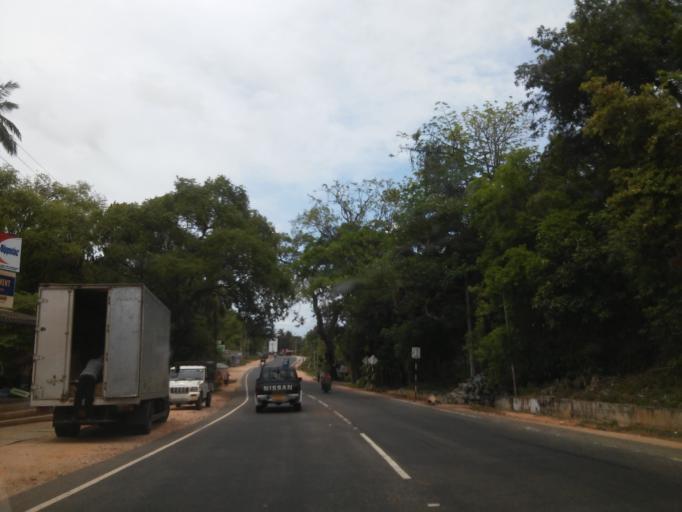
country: LK
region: Eastern Province
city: Trincomalee
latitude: 8.5878
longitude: 81.1971
